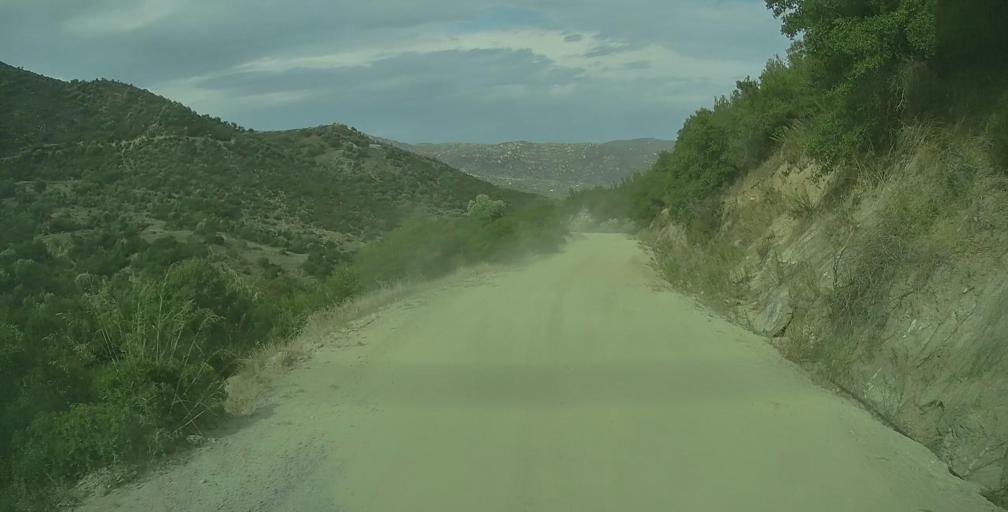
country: GR
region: Central Macedonia
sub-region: Nomos Chalkidikis
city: Sykia
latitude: 40.0181
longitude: 23.9387
